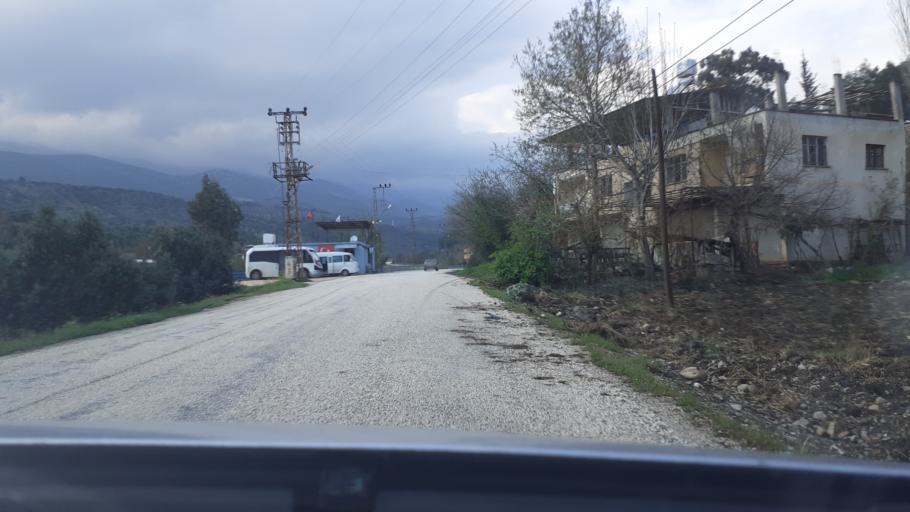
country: TR
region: Hatay
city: Kirikhan
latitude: 36.5055
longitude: 36.3231
